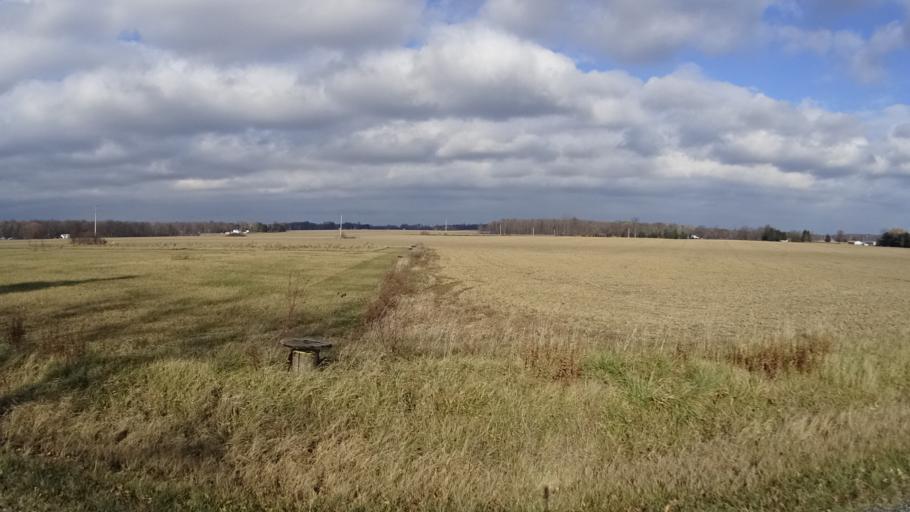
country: US
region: Ohio
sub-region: Lorain County
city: Camden
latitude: 41.2882
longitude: -82.2773
